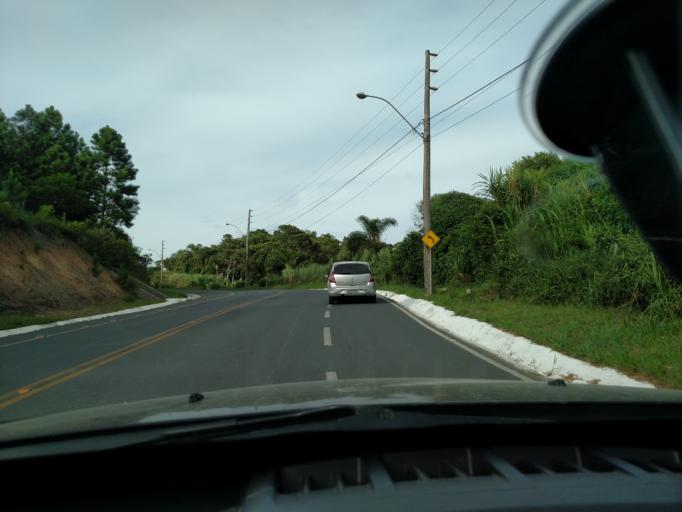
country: BR
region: Santa Catarina
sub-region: Porto Belo
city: Porto Belo
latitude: -27.1603
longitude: -48.4932
